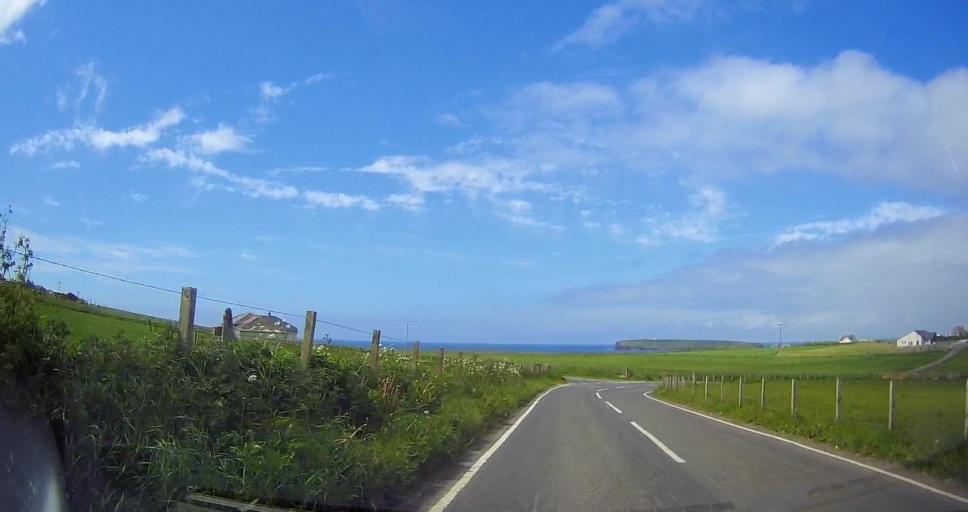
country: GB
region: Scotland
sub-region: Orkney Islands
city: Stromness
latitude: 59.1167
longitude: -3.3047
